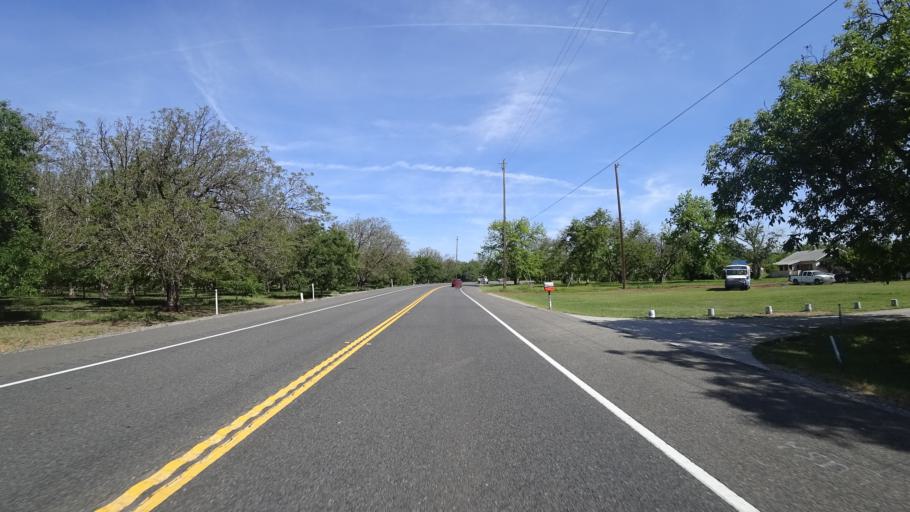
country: US
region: California
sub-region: Tehama County
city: Red Bluff
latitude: 40.1676
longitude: -122.1579
